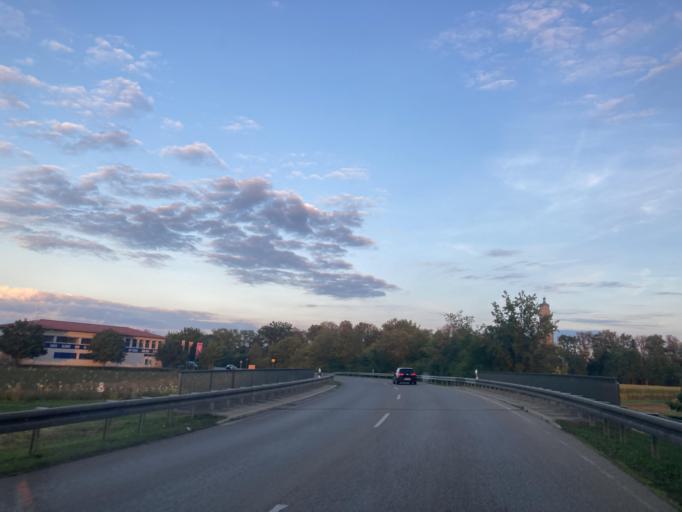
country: DE
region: Bavaria
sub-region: Swabia
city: Noerdlingen
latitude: 48.8537
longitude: 10.4802
